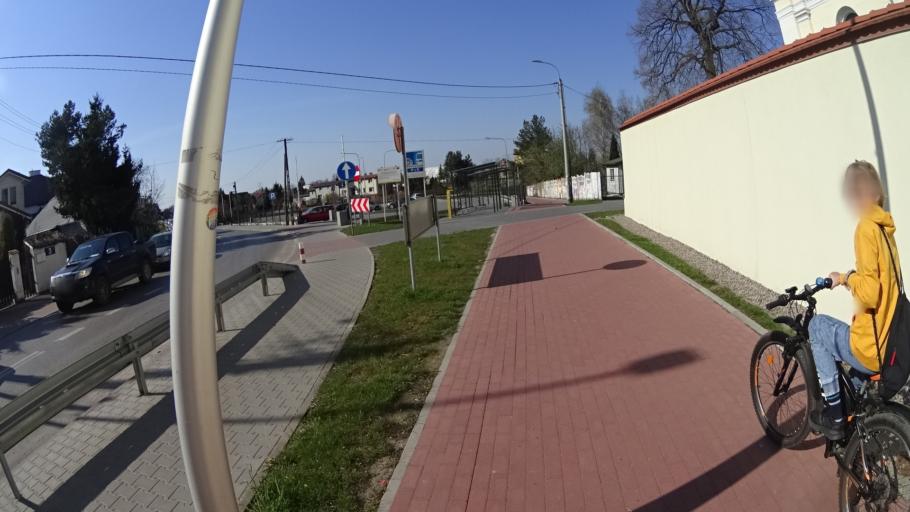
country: PL
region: Masovian Voivodeship
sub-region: Powiat warszawski zachodni
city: Babice
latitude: 52.2513
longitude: 20.8412
